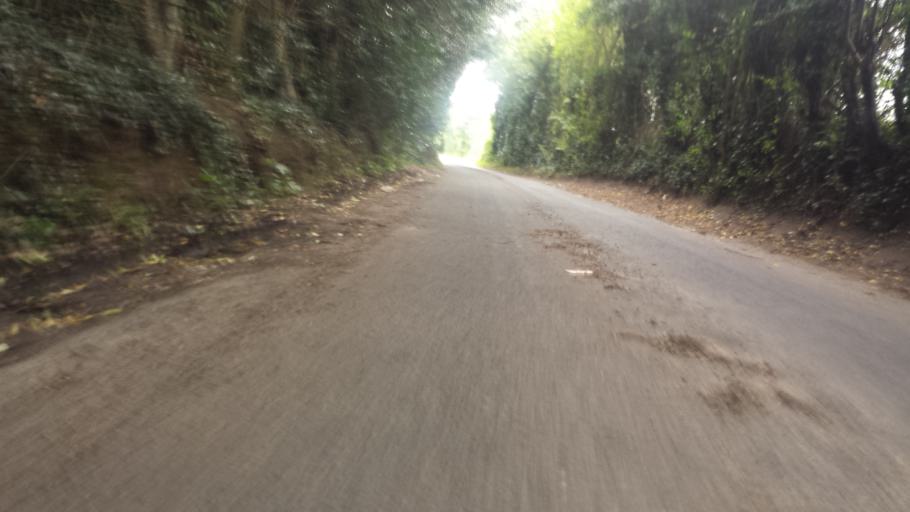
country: GB
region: England
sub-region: Kent
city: Swanley
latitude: 51.3772
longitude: 0.1600
